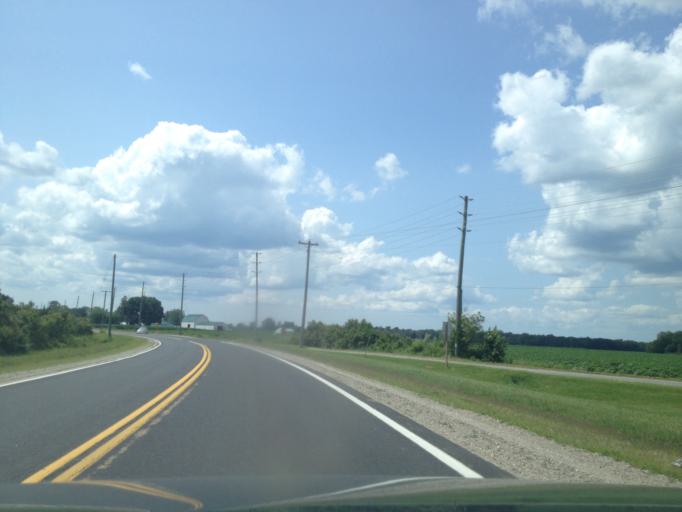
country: CA
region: Ontario
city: Aylmer
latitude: 42.6614
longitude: -80.8114
